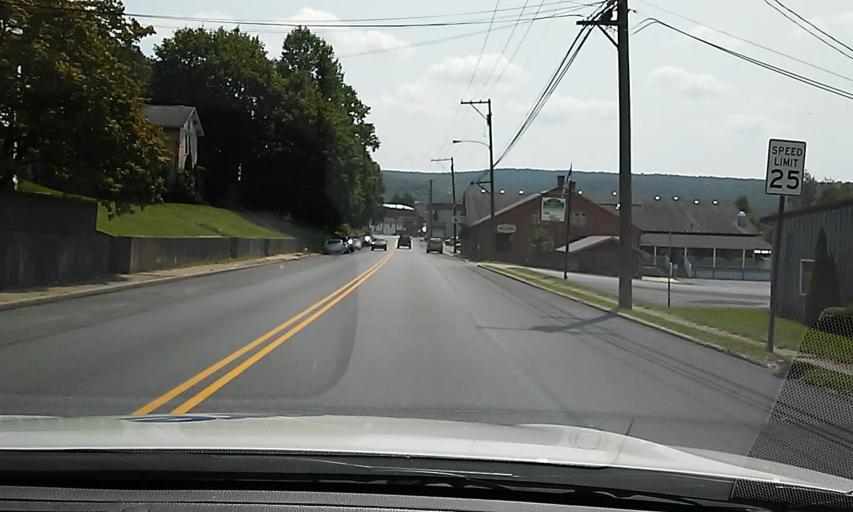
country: US
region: Pennsylvania
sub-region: Elk County
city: Ridgway
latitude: 41.4278
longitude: -78.7330
